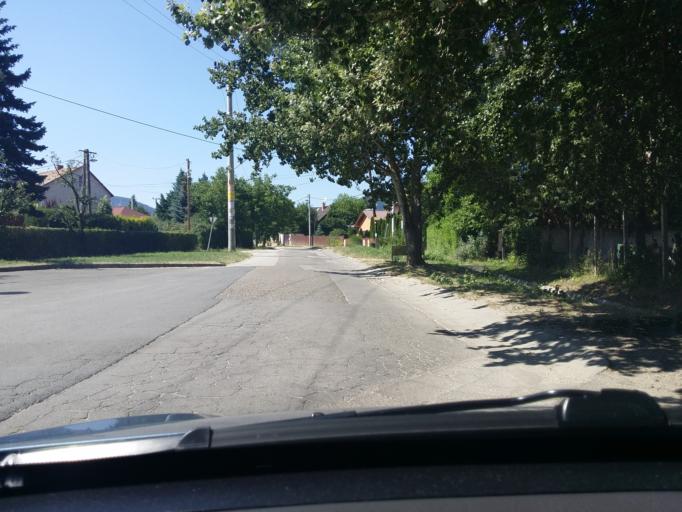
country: HU
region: Pest
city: Nagykovacsi
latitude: 47.6537
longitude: 19.0226
